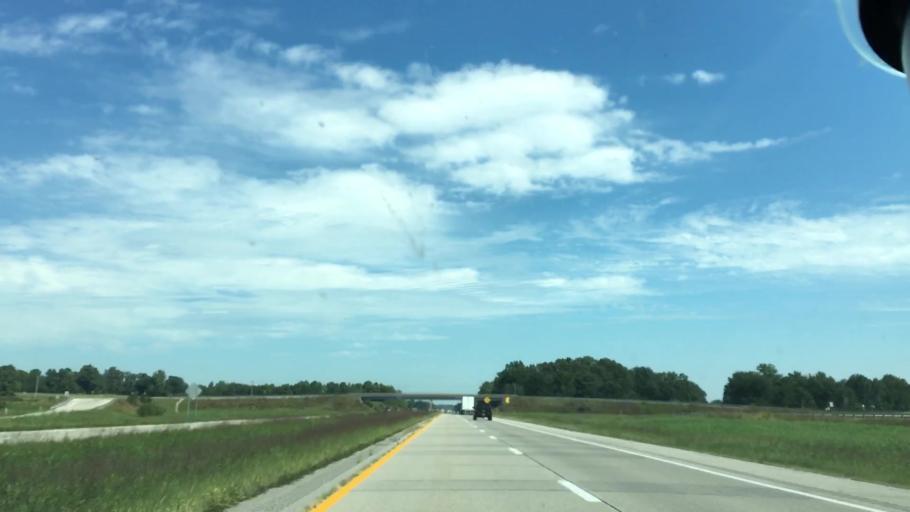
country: US
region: Kentucky
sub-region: Daviess County
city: Owensboro
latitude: 37.7556
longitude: -87.2641
